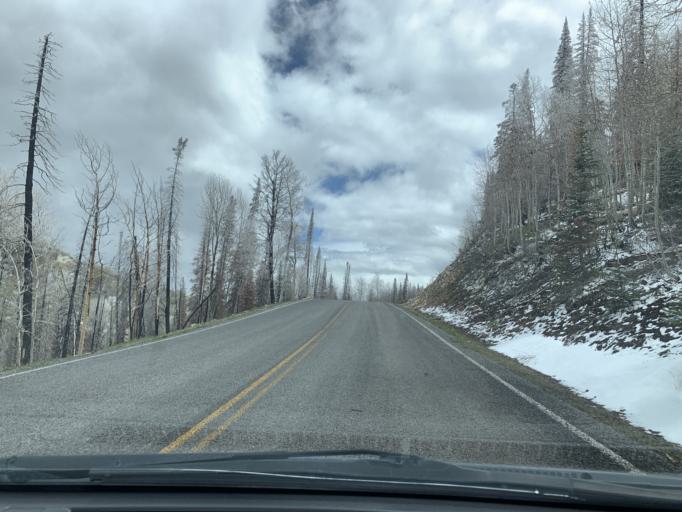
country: US
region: Utah
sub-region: Utah County
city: Santaquin
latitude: 39.8630
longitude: -111.6909
